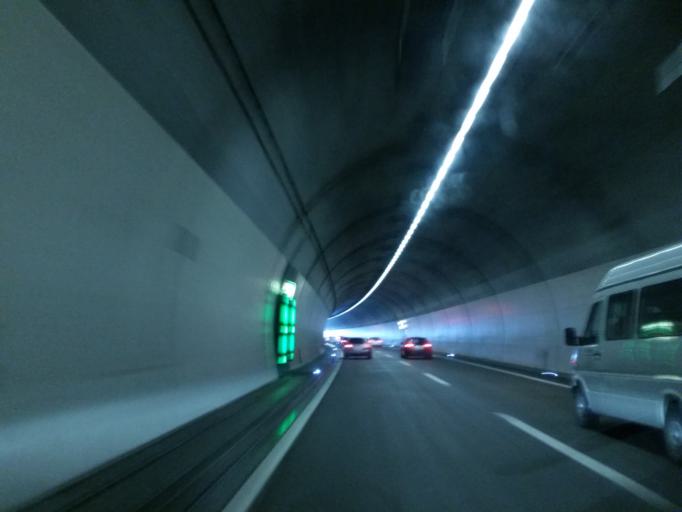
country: CH
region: Saint Gallen
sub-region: Wahlkreis Sarganserland
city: Walenstadt
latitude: 47.1098
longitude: 9.2866
